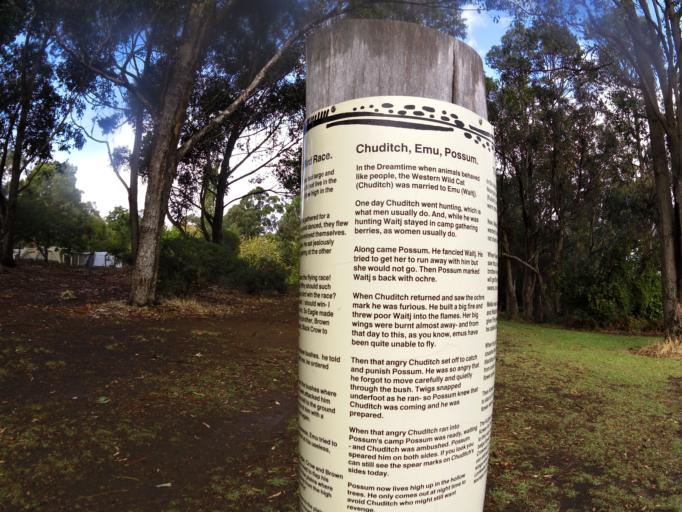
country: AU
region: Western Australia
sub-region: Donnybrook-Balingup
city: Donnybrook
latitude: -33.5753
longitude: 115.8267
